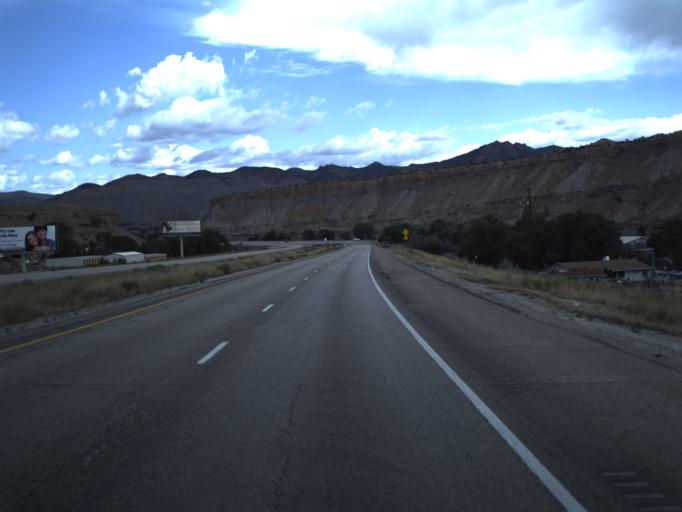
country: US
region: Utah
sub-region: Carbon County
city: Spring Glen
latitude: 39.6360
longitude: -110.8611
